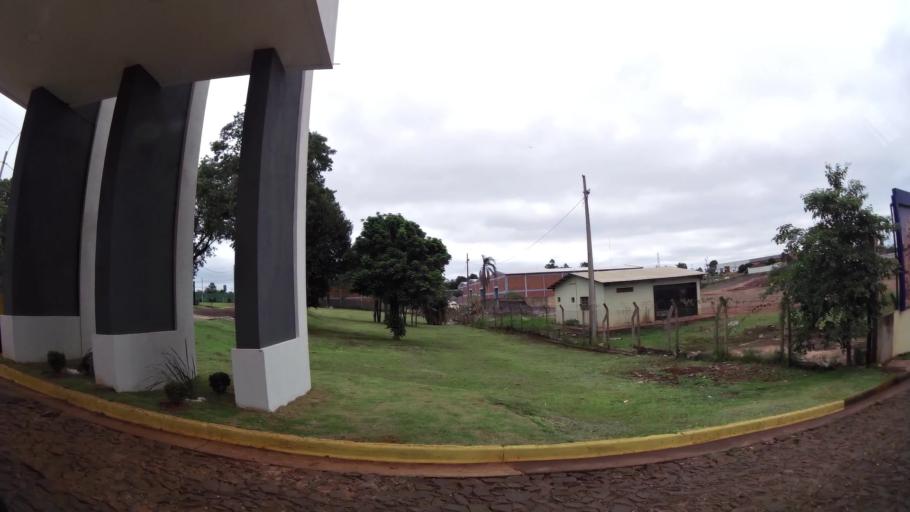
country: PY
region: Alto Parana
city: Ciudad del Este
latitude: -25.4986
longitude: -54.6796
